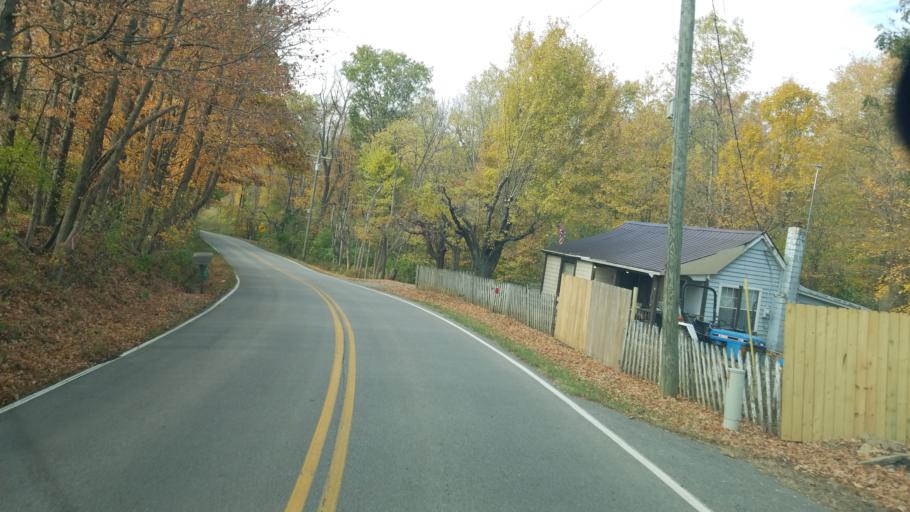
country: US
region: Ohio
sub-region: Warren County
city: Morrow
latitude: 39.4186
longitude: -84.0812
